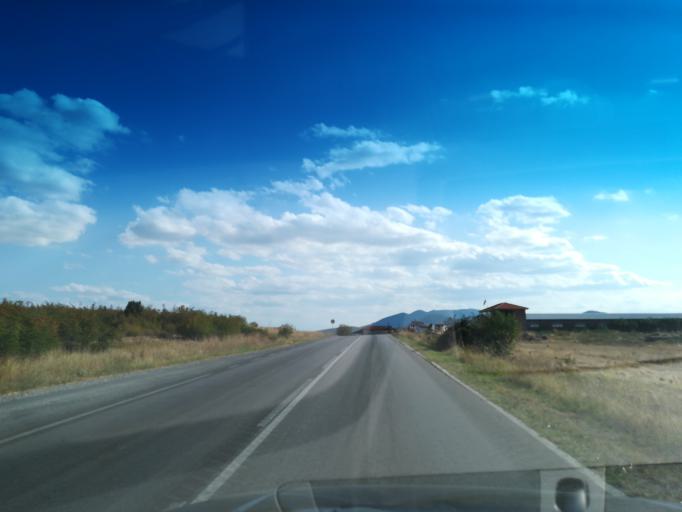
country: BG
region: Khaskovo
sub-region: Obshtina Mineralni Bani
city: Mineralni Bani
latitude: 41.9749
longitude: 25.3521
